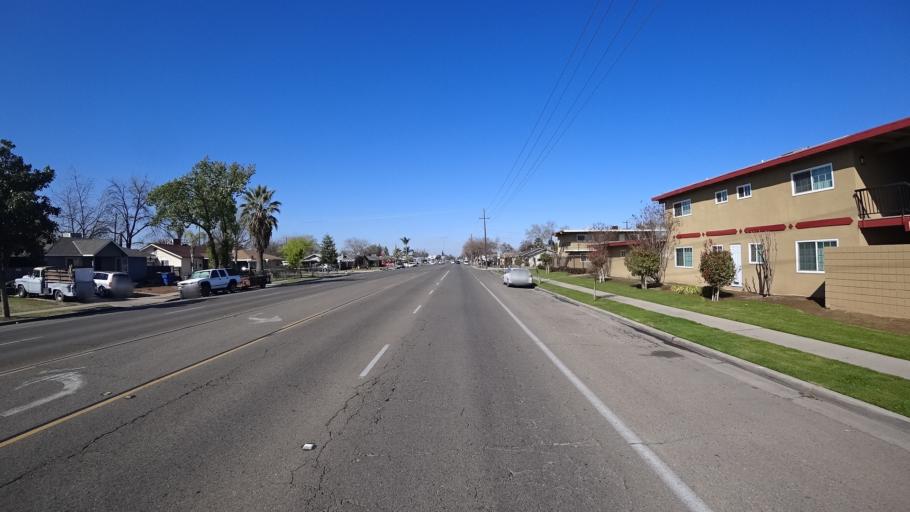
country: US
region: California
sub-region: Fresno County
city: Fresno
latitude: 36.7794
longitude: -119.8215
